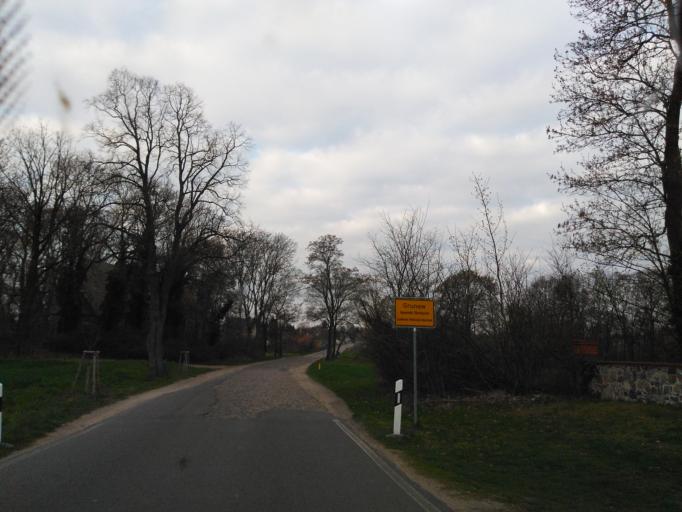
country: DE
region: Brandenburg
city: Buckow
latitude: 52.6077
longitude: 14.0379
